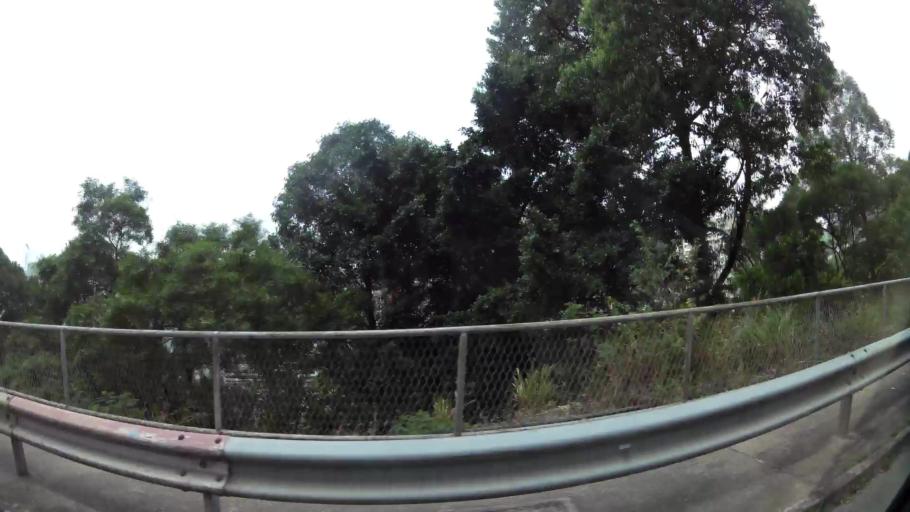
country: HK
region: Sham Shui Po
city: Sham Shui Po
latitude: 22.3420
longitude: 114.1595
